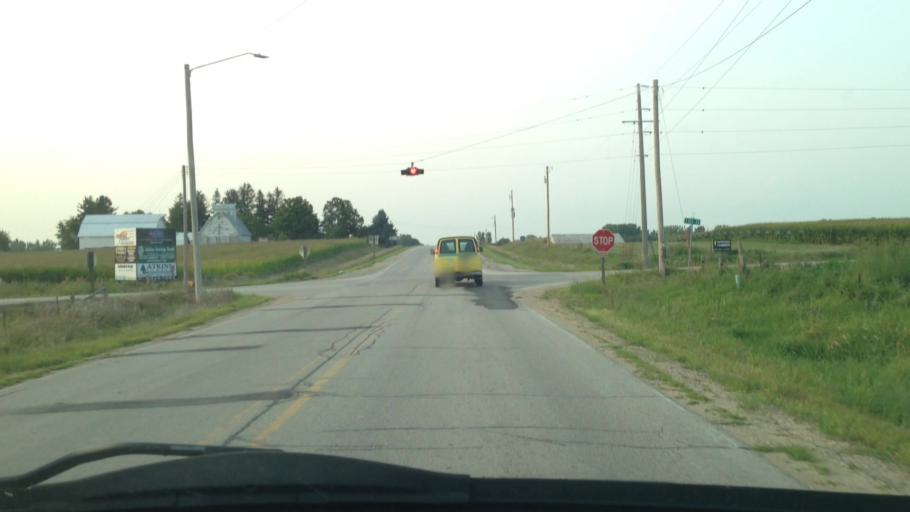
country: US
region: Iowa
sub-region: Benton County
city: Atkins
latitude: 41.9921
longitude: -91.8732
